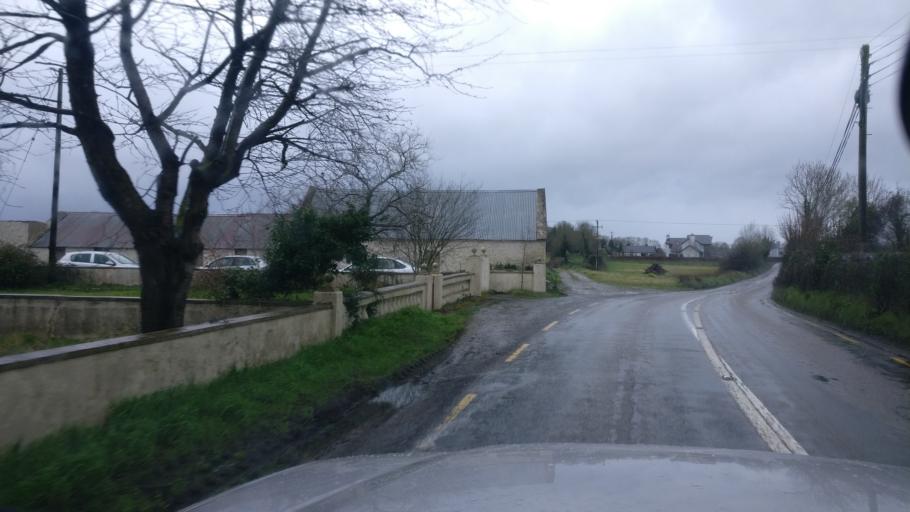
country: IE
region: Connaught
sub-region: County Galway
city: Portumna
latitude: 53.0933
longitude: -8.2632
